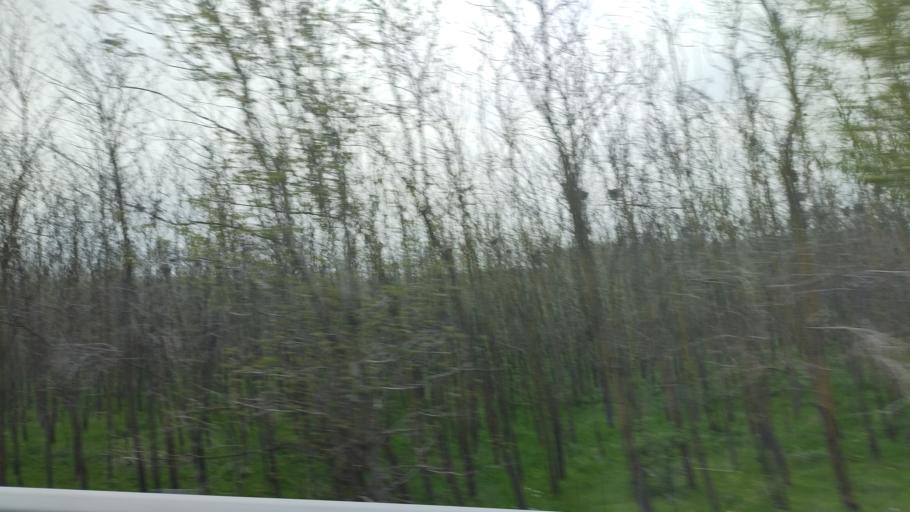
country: RO
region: Constanta
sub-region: Comuna Deleni
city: Pietreni
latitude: 44.0901
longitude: 28.0805
